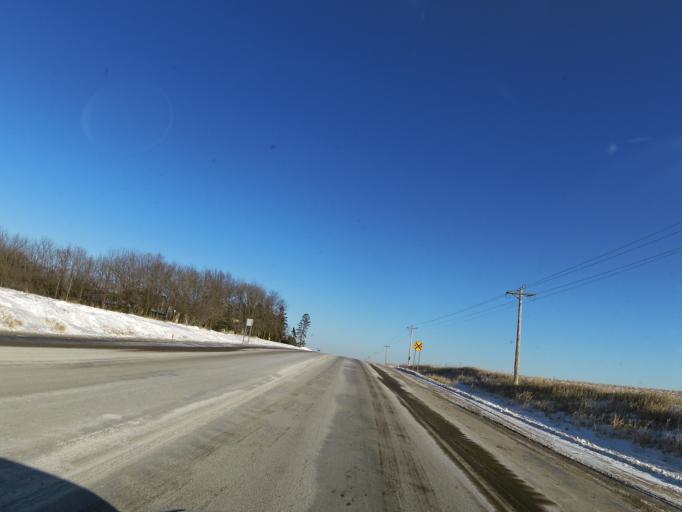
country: US
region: Minnesota
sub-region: Le Sueur County
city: Montgomery
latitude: 44.4861
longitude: -93.5849
